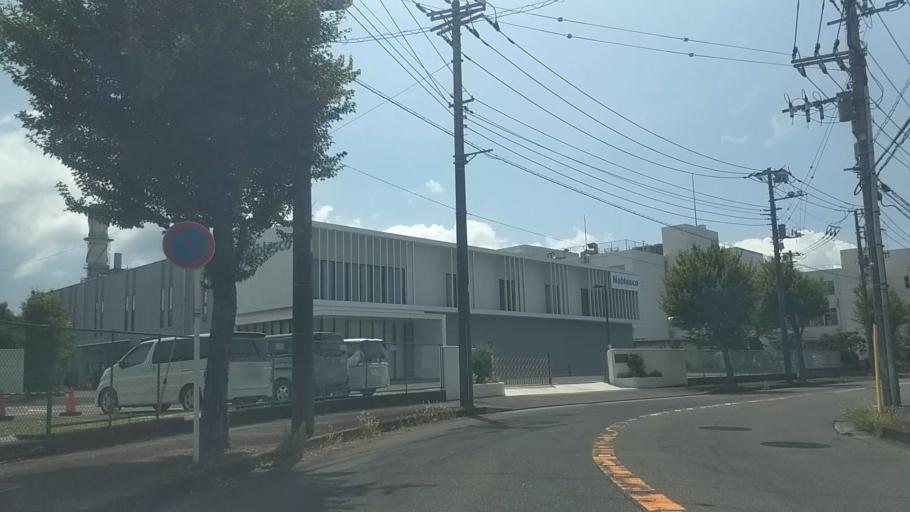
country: JP
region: Kanagawa
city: Yokosuka
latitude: 35.3124
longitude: 139.6419
